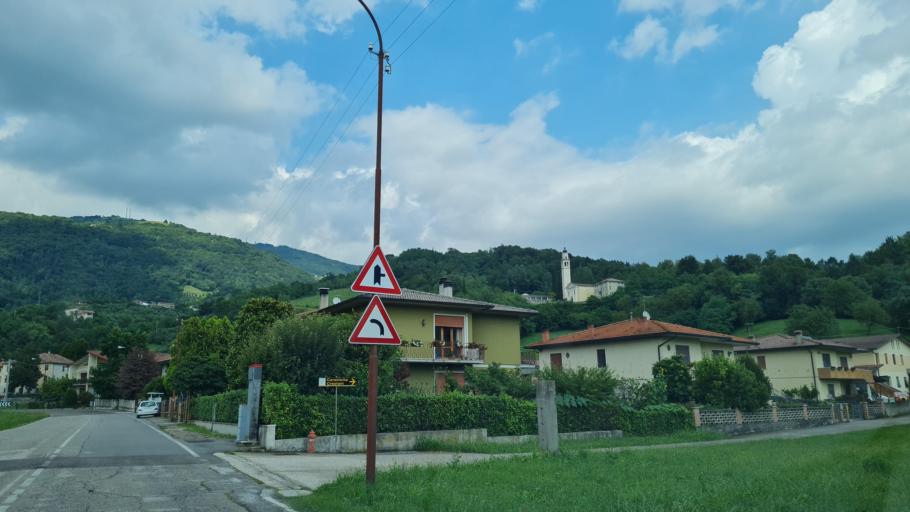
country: IT
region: Veneto
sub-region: Provincia di Vicenza
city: Marostica
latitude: 45.7669
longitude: 11.6607
